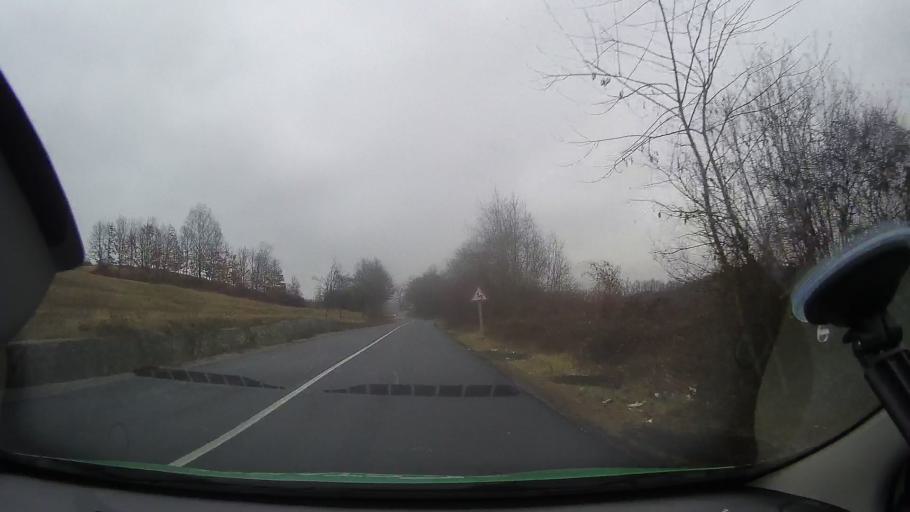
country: RO
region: Arad
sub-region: Comuna Varfurile
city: Varfurile
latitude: 46.3266
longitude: 22.4928
